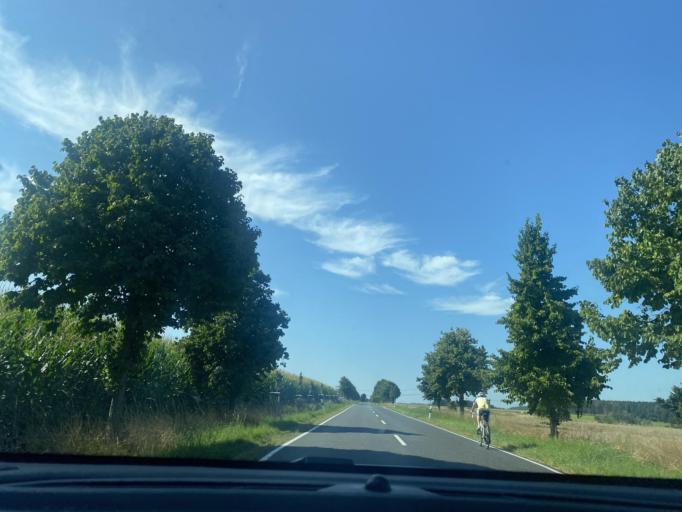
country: DE
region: Saxony
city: Bernstadt
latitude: 51.0387
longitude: 14.8173
